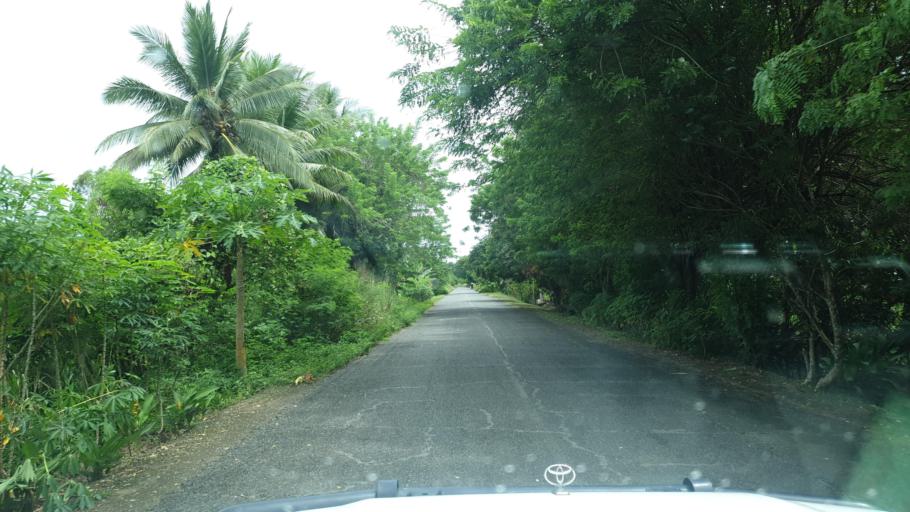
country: PG
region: Gulf
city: Kerema
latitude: -8.1186
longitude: 146.1709
